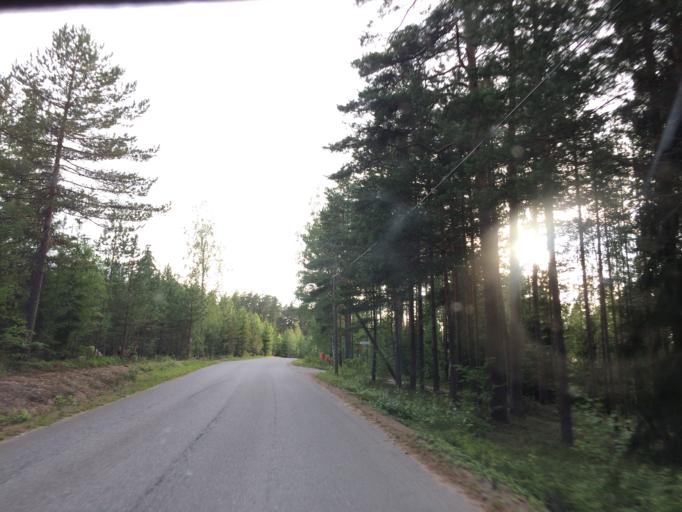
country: FI
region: Haeme
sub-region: Haemeenlinna
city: Janakkala
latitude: 60.8557
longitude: 24.6074
